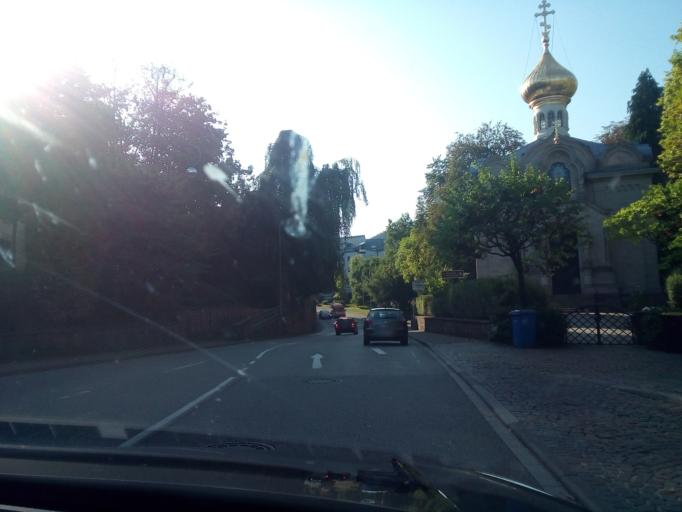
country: DE
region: Baden-Wuerttemberg
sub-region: Karlsruhe Region
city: Baden-Baden
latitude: 48.7545
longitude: 8.2444
